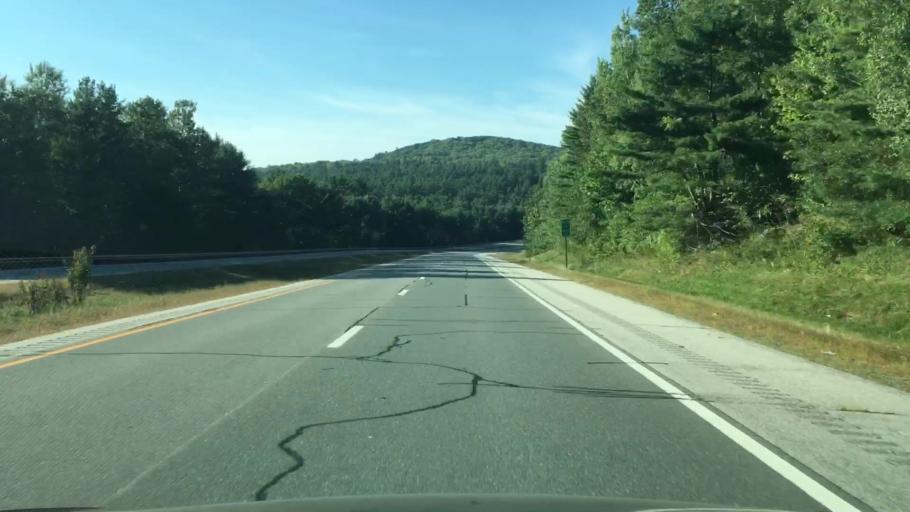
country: US
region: New Hampshire
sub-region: Grafton County
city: Littleton
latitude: 44.2438
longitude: -71.7595
